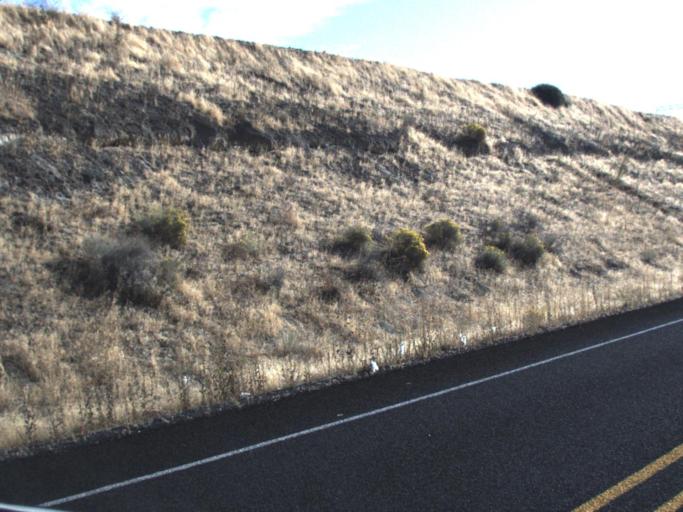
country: US
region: Washington
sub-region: Franklin County
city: Connell
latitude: 46.6210
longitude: -118.7131
